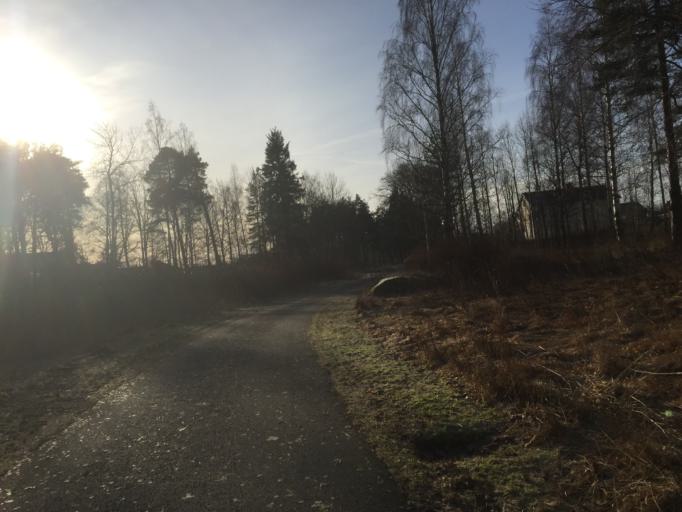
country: SE
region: Joenkoeping
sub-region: Aneby Kommun
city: Aneby
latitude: 57.8365
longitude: 14.8142
